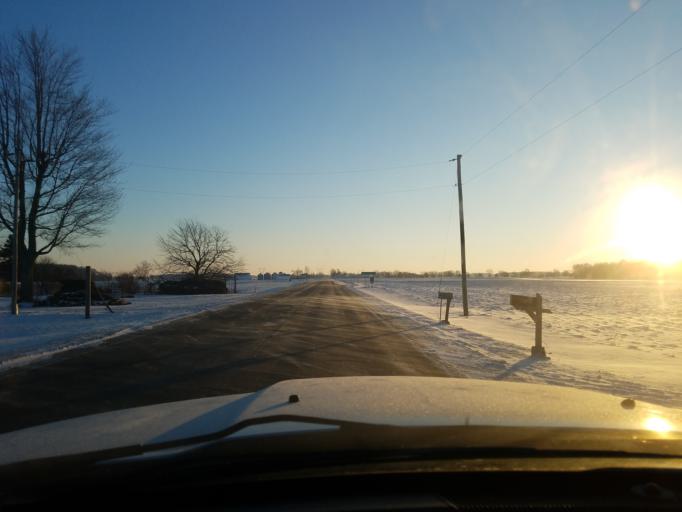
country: US
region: Indiana
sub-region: Marshall County
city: Bremen
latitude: 41.4497
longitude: -86.2552
